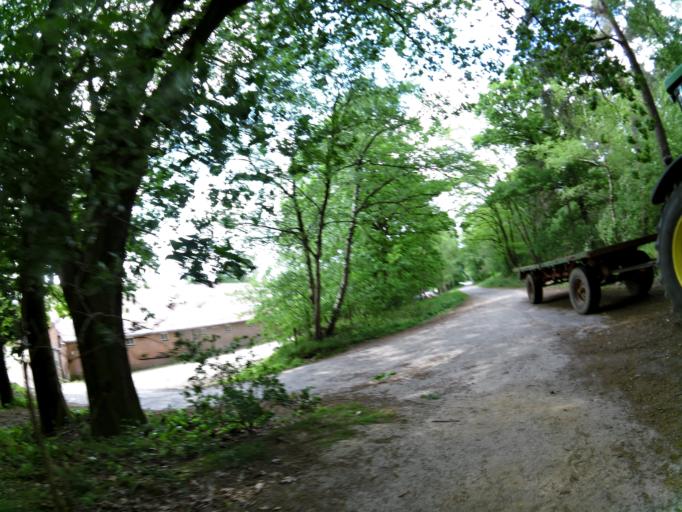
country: NL
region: Limburg
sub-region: Gemeente Brunssum
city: Brunssum
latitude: 50.9345
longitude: 5.9971
